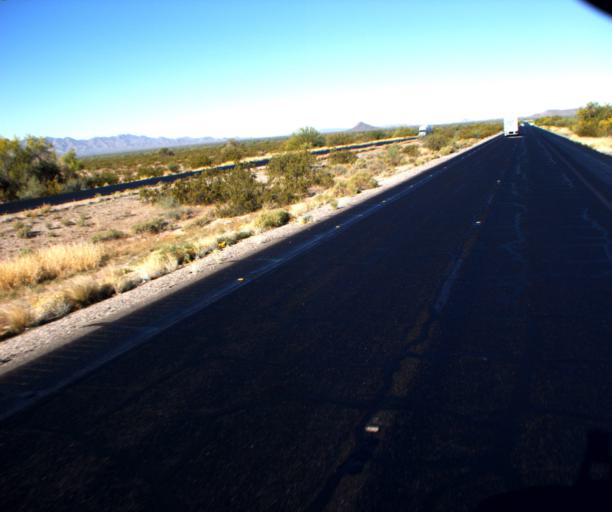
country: US
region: Arizona
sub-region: Pinal County
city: Maricopa
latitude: 32.8395
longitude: -112.2317
